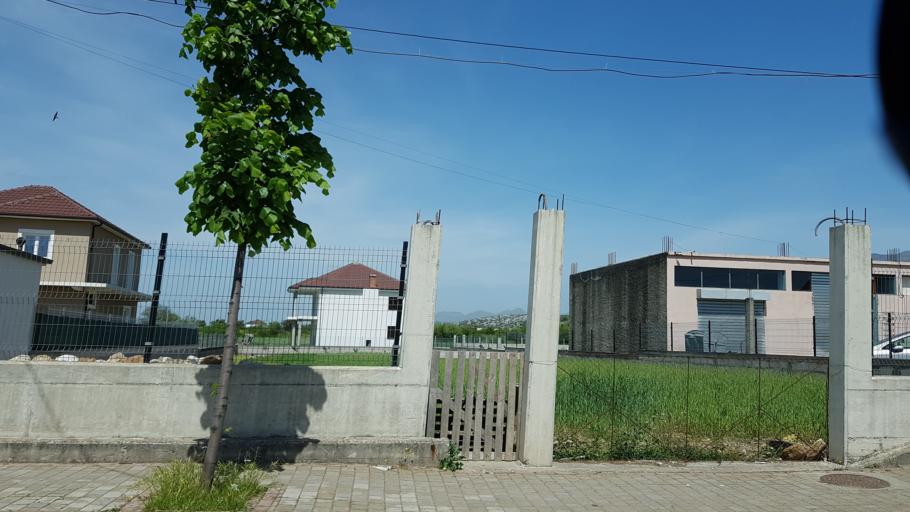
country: AL
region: Shkoder
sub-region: Rrethi i Shkodres
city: Guri i Zi
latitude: 42.1117
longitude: 19.5697
